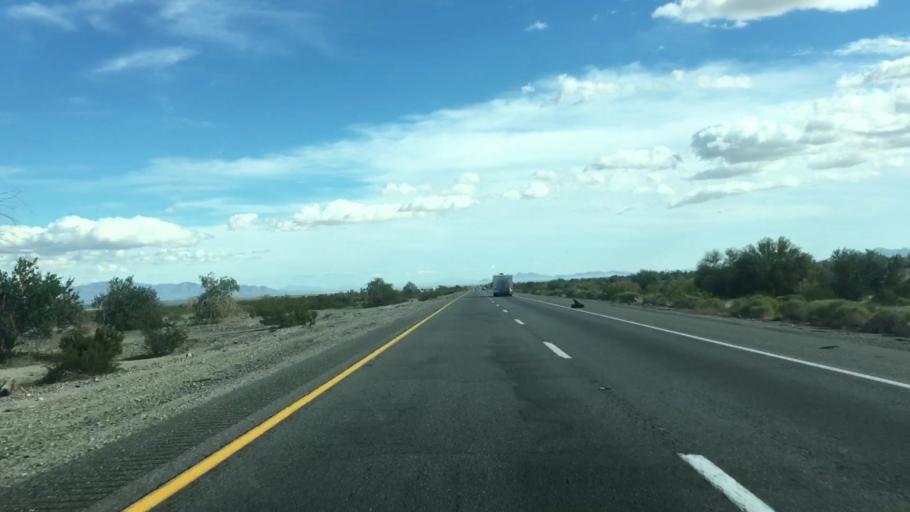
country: US
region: California
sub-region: Riverside County
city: Mesa Verde
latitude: 33.6743
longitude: -115.2168
